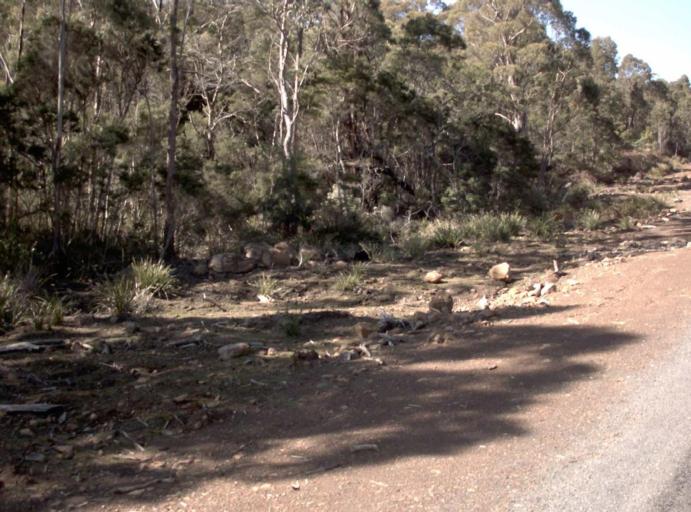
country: AU
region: Tasmania
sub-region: Launceston
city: Mayfield
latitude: -41.3170
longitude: 147.1155
